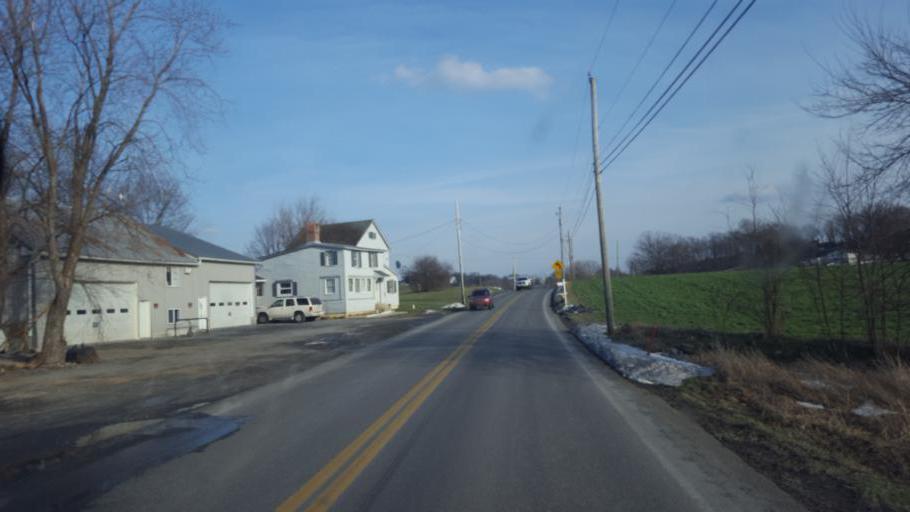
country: US
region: Pennsylvania
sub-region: Lancaster County
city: Intercourse
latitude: 40.0511
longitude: -76.1249
